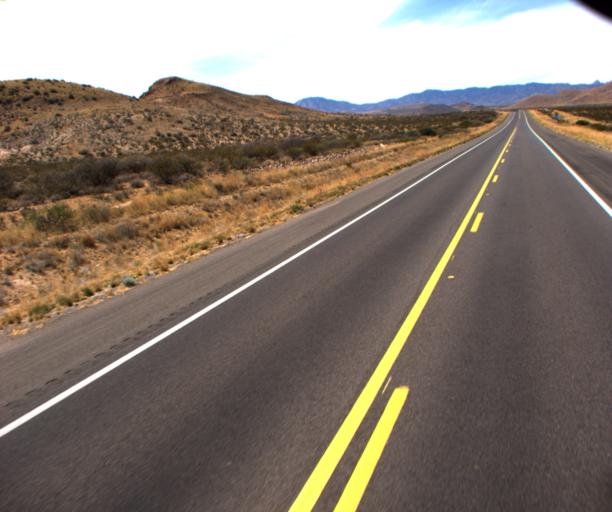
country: US
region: Arizona
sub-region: Cochise County
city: Willcox
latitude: 31.9056
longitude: -109.7449
